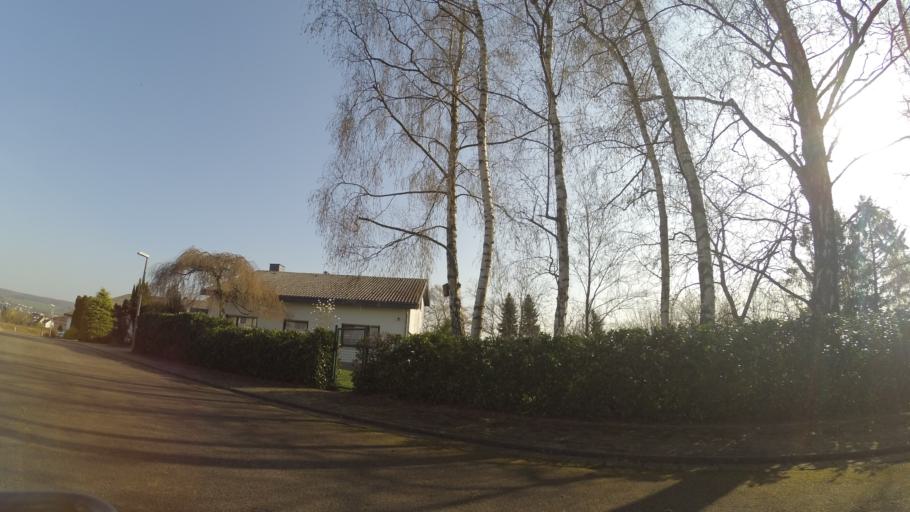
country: DE
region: Saarland
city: Heusweiler
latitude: 49.3435
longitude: 6.9144
